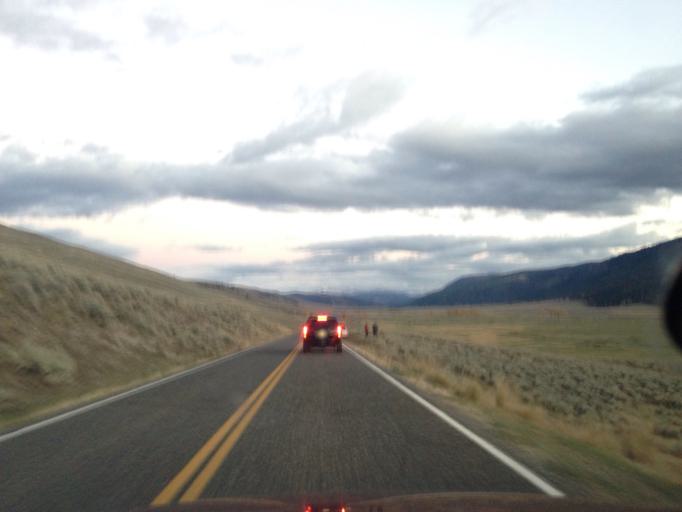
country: US
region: Montana
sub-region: Park County
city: Livingston
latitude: 44.9058
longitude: -110.2489
